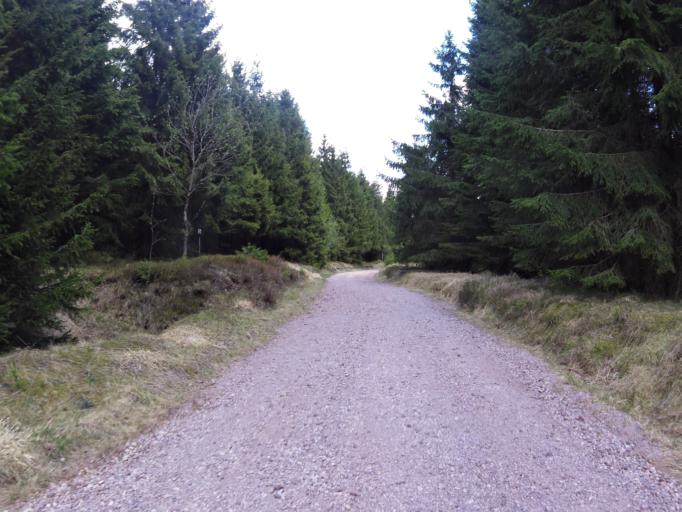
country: DE
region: Thuringia
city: Zella-Mehlis
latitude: 50.7085
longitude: 10.6713
